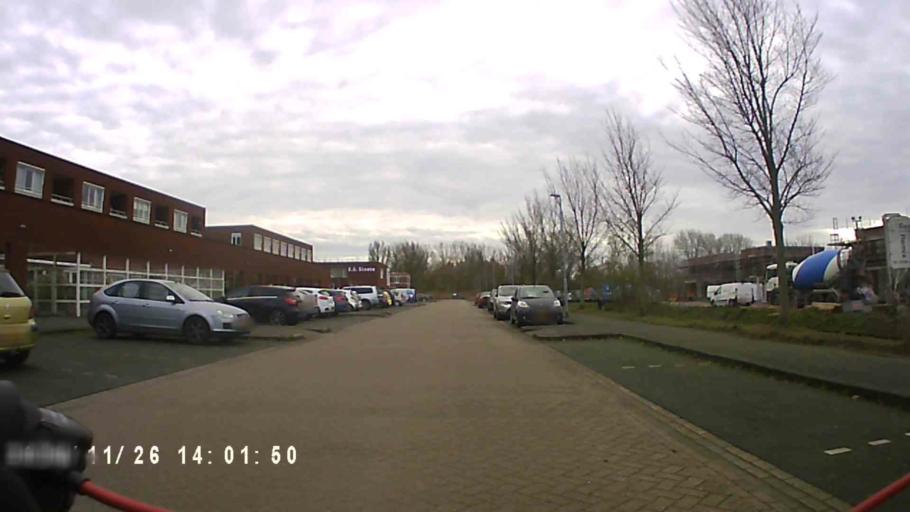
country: NL
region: Groningen
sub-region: Gemeente Delfzijl
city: Delfzijl
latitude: 53.3346
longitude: 6.9096
